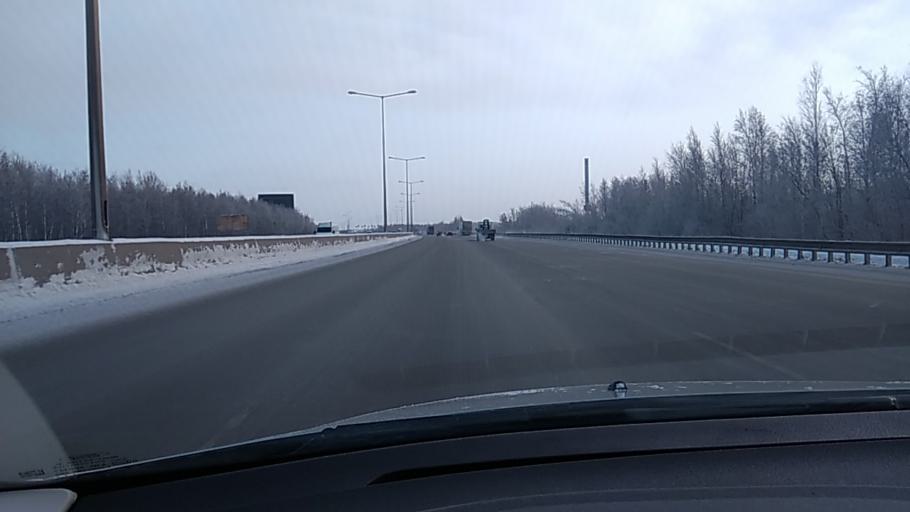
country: RU
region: Sverdlovsk
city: Istok
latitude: 56.7652
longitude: 60.7457
